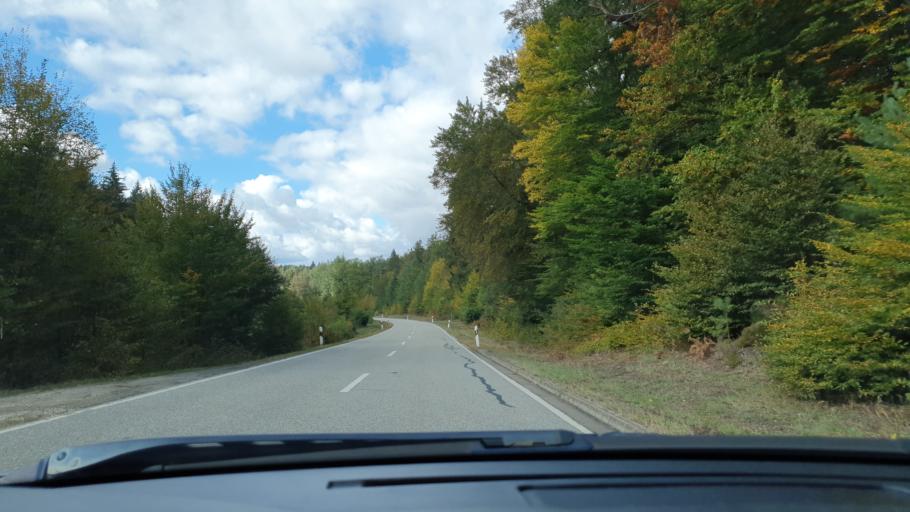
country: DE
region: Rheinland-Pfalz
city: Waldleiningen
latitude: 49.4163
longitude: 7.8256
